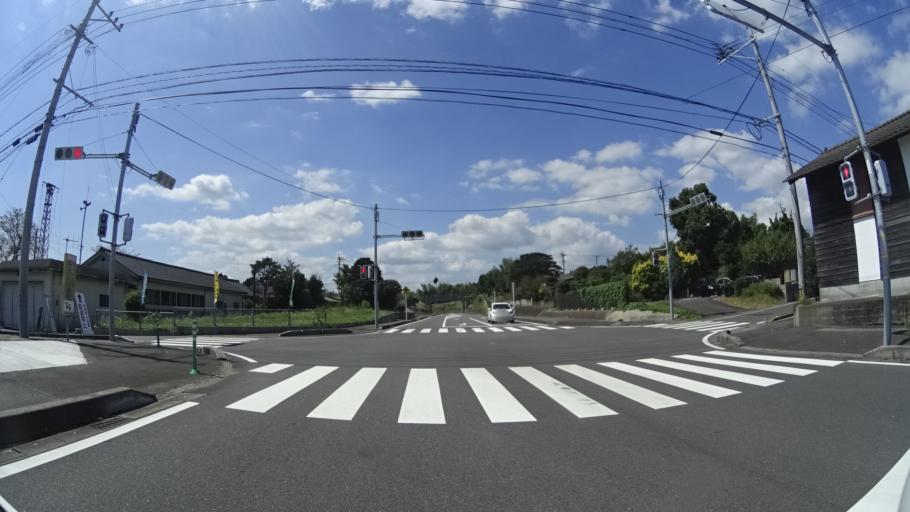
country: JP
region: Kagoshima
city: Kajiki
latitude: 31.8148
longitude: 130.7027
